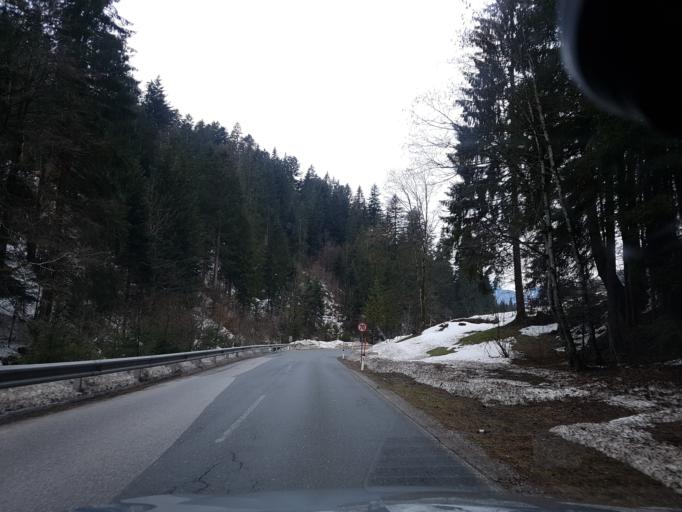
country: AT
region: Tyrol
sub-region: Politischer Bezirk Kufstein
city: Worgl
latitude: 47.4631
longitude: 12.0904
